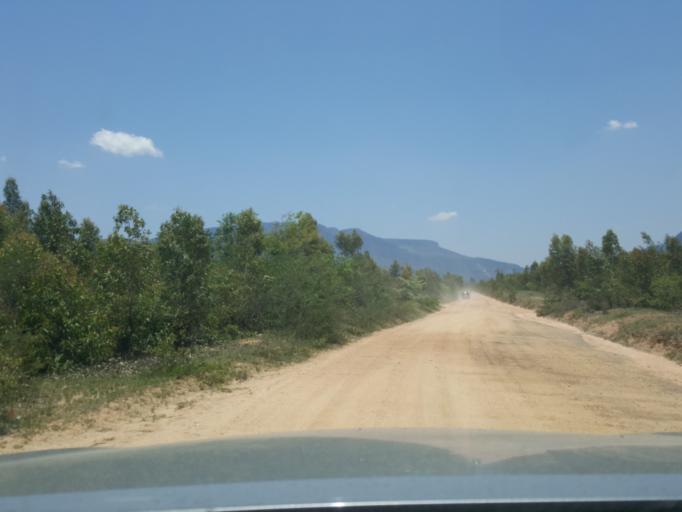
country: ZA
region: Limpopo
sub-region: Mopani District Municipality
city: Hoedspruit
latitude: -24.5862
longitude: 30.9728
